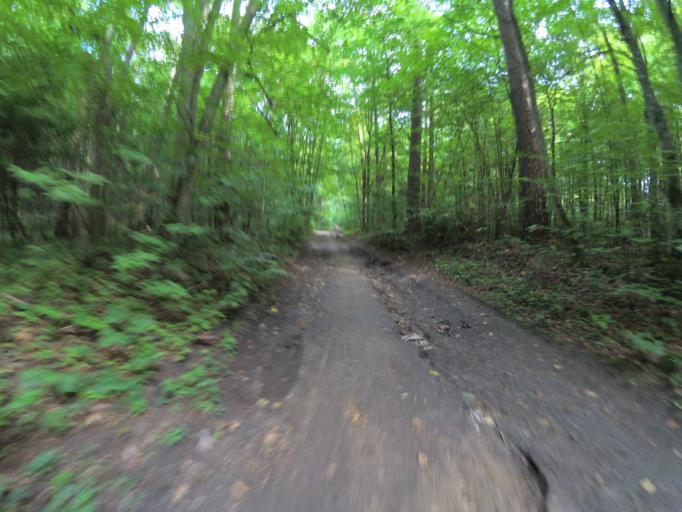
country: PL
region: Pomeranian Voivodeship
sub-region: Gdynia
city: Wielki Kack
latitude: 54.4891
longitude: 18.4499
